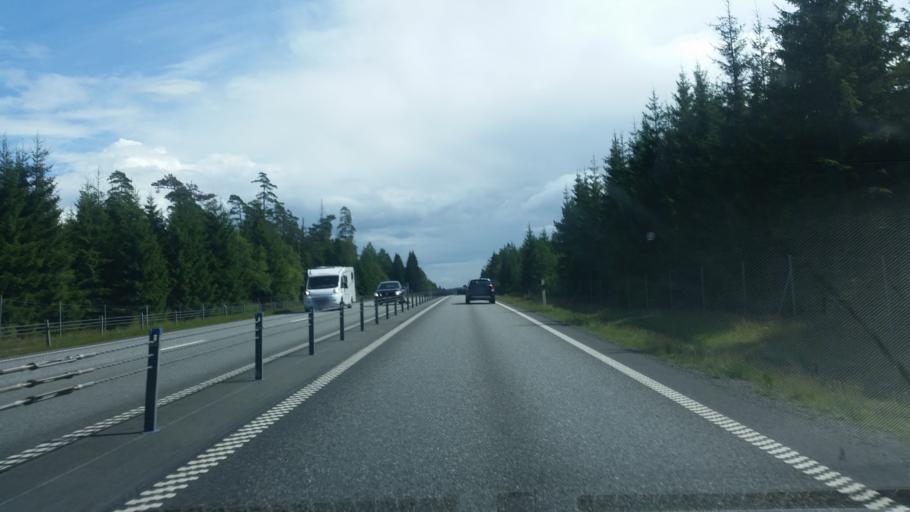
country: SE
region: Joenkoeping
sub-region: Mullsjo Kommun
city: Mullsjoe
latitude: 57.7657
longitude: 13.7540
